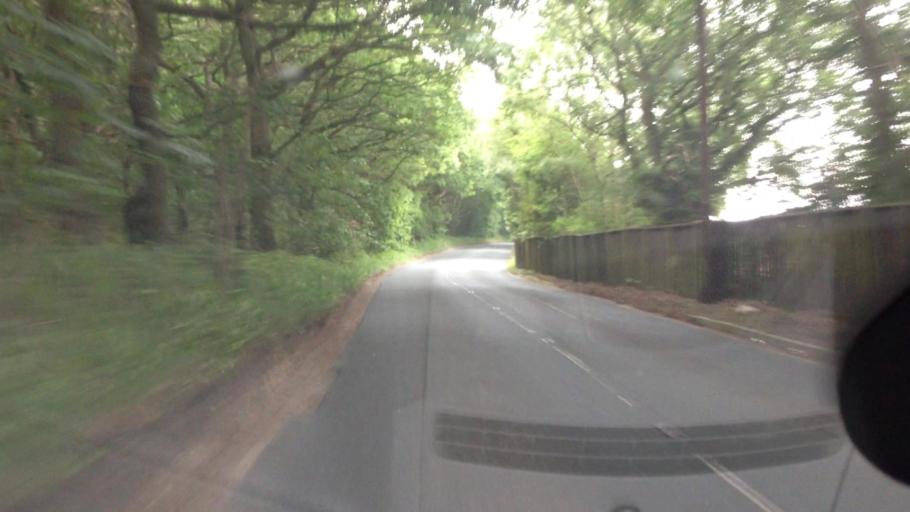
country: GB
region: England
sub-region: City and Borough of Wakefield
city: Woolley
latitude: 53.6173
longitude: -1.5389
